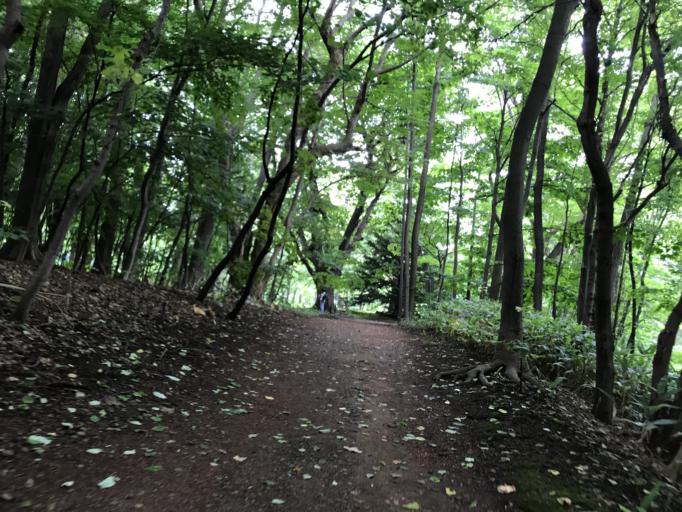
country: JP
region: Hokkaido
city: Sapporo
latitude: 43.0651
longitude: 141.3415
